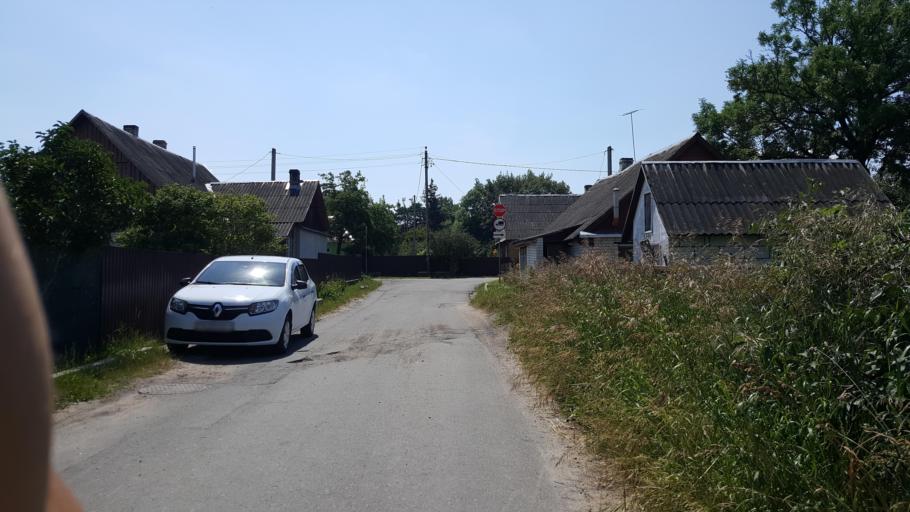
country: BY
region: Brest
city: Kamyanyets
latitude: 52.4064
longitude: 23.8272
